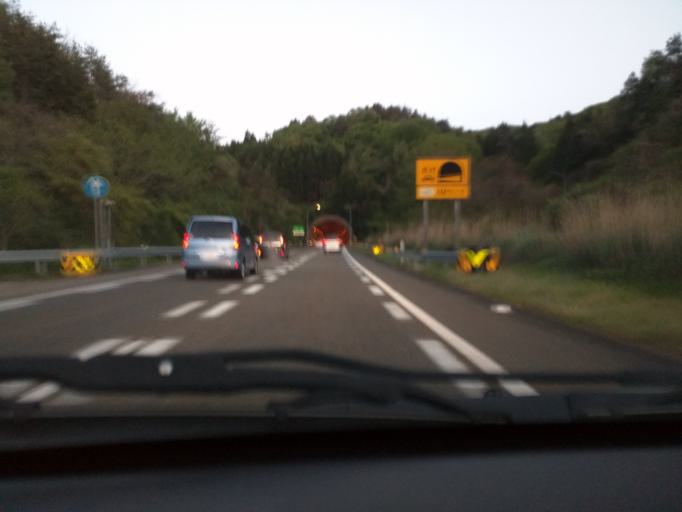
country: JP
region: Niigata
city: Kashiwazaki
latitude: 37.3443
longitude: 138.5142
